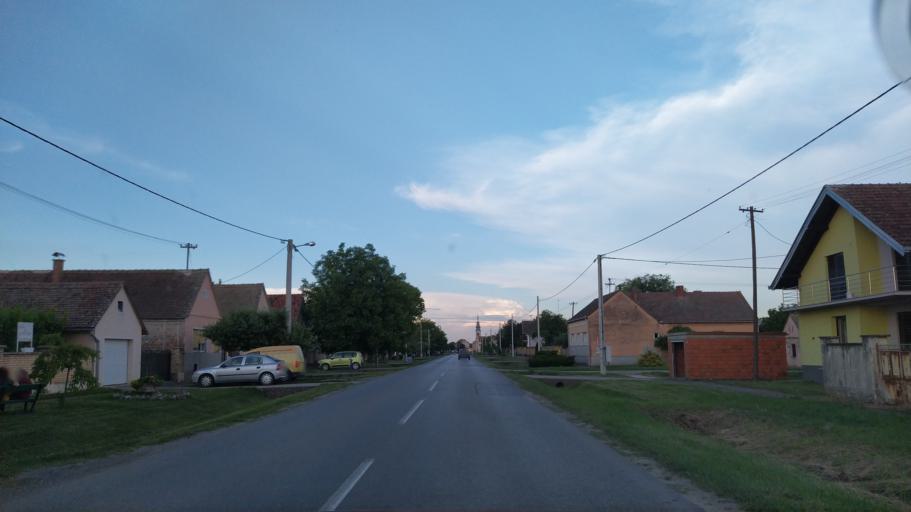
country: HR
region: Osjecko-Baranjska
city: Gorjani
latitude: 45.4608
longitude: 18.3163
